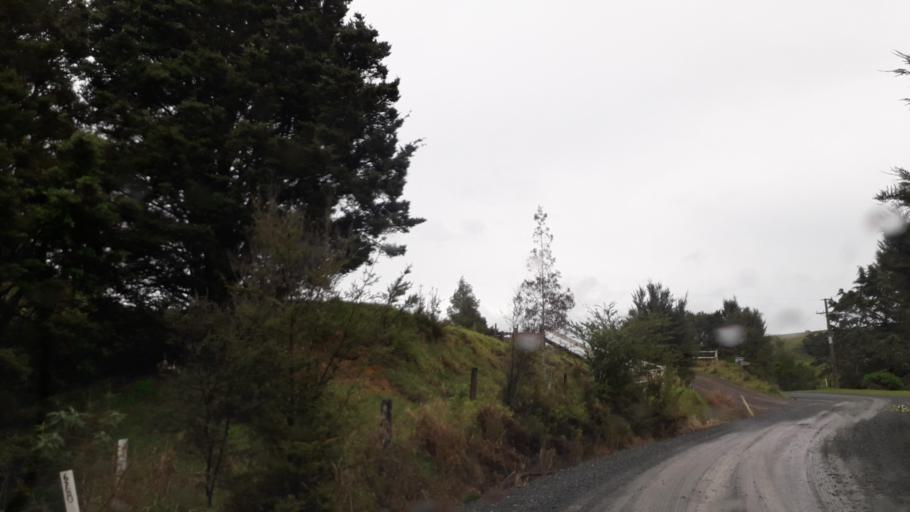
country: NZ
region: Northland
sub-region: Far North District
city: Kerikeri
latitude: -35.1318
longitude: 173.7305
